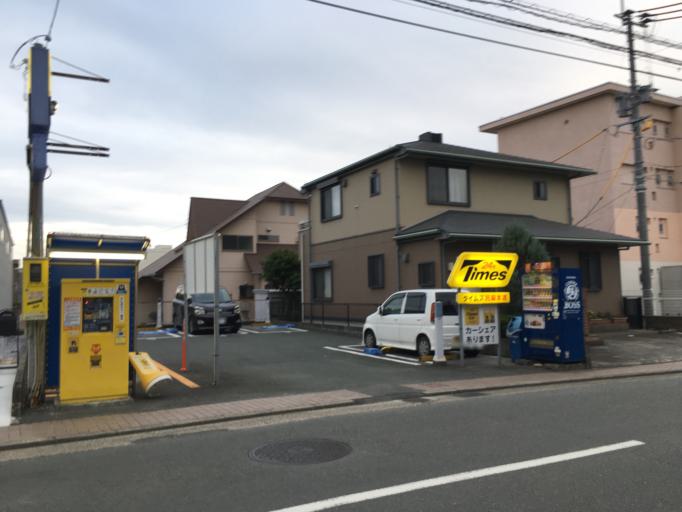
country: JP
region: Kumamoto
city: Kumamoto
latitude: 32.8050
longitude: 130.7325
